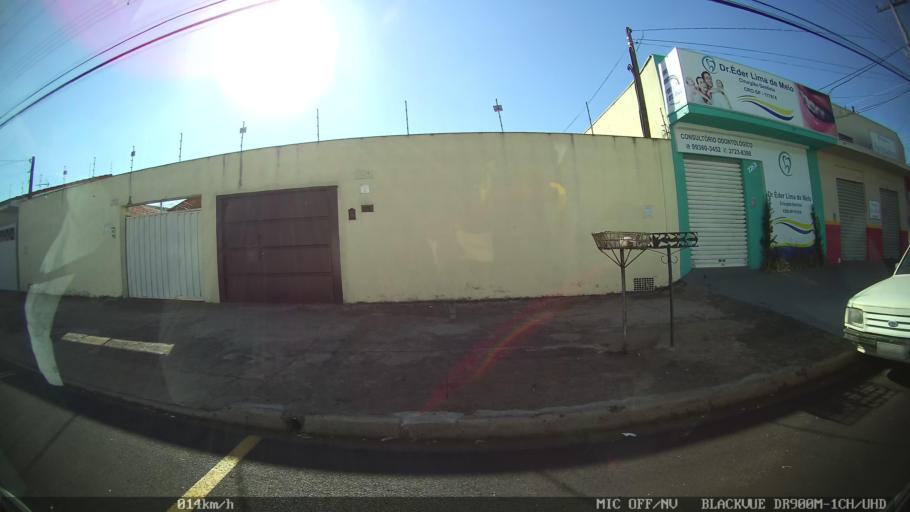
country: BR
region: Sao Paulo
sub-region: Franca
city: Franca
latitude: -20.5108
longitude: -47.4209
